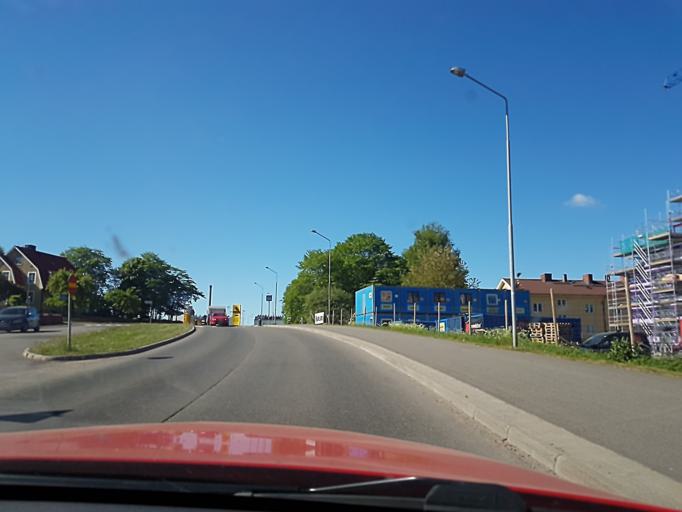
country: SE
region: Vaestra Goetaland
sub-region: Skovde Kommun
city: Skoevde
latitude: 58.3886
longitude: 13.8605
